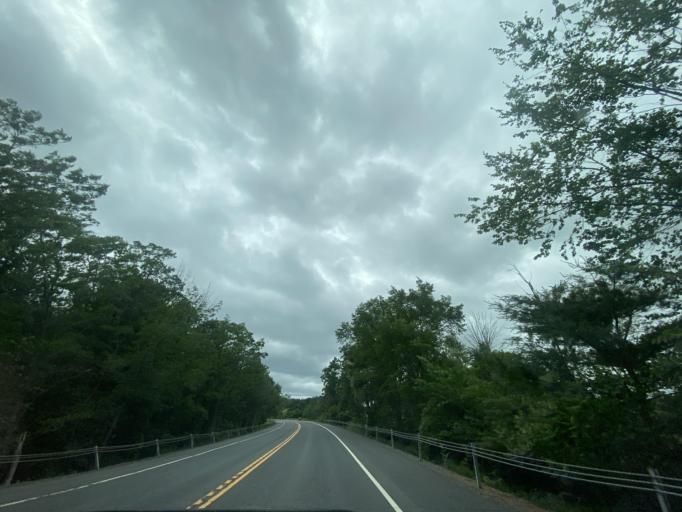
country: US
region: New York
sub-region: Greene County
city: Cairo
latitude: 42.3944
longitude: -73.9572
